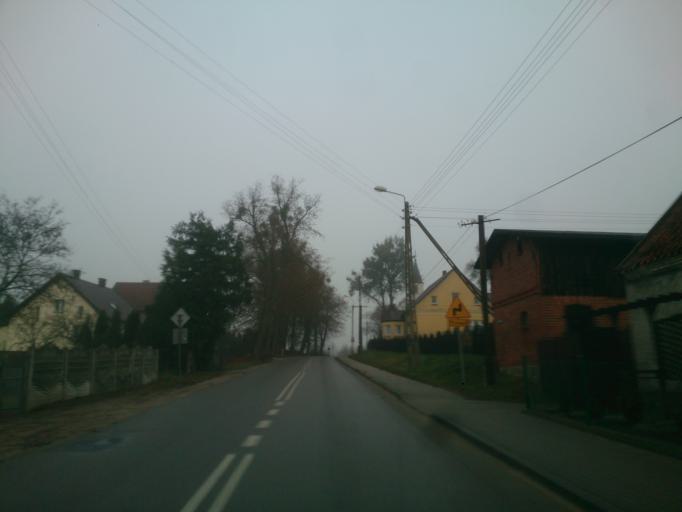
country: PL
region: Pomeranian Voivodeship
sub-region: Powiat starogardzki
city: Zblewo
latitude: 53.8892
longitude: 18.3507
